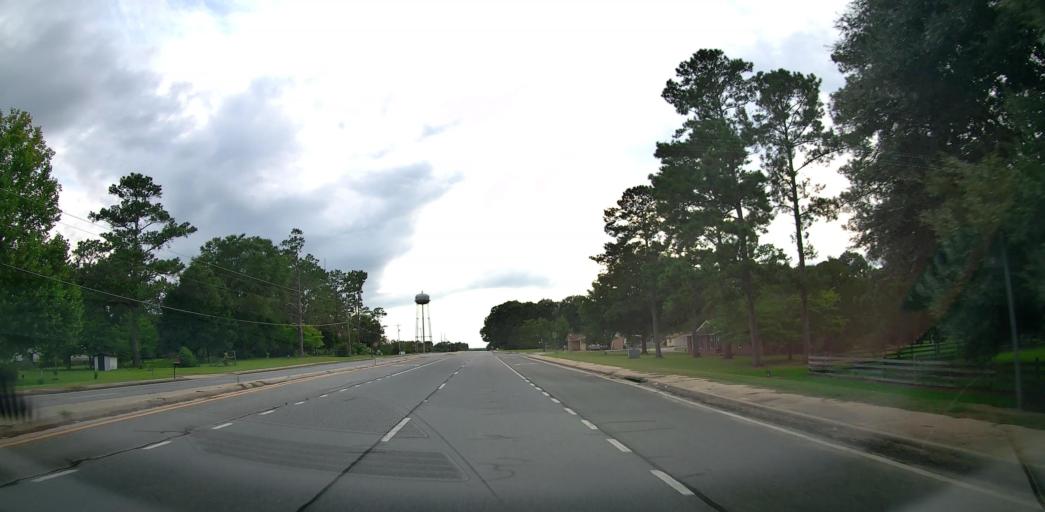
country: US
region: Georgia
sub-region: Pulaski County
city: Hawkinsville
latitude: 32.2814
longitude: -83.4362
